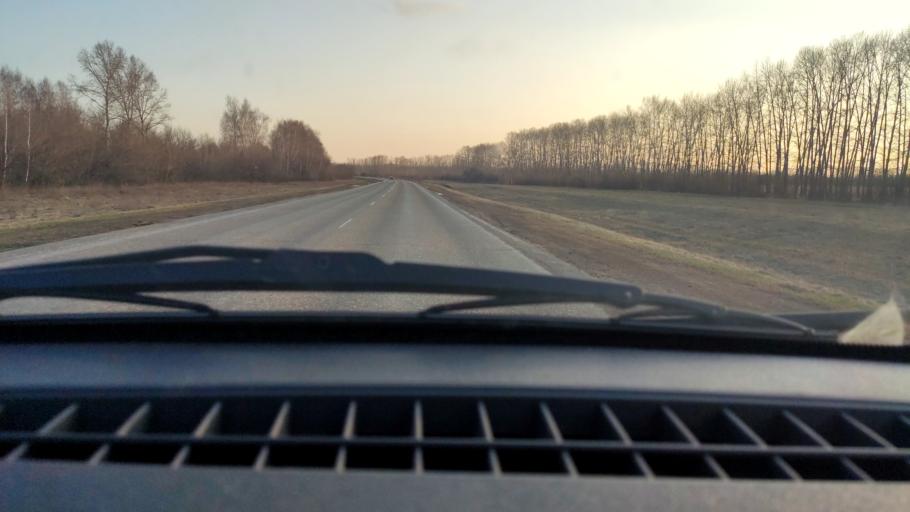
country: RU
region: Bashkortostan
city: Davlekanovo
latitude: 54.3540
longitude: 55.1836
